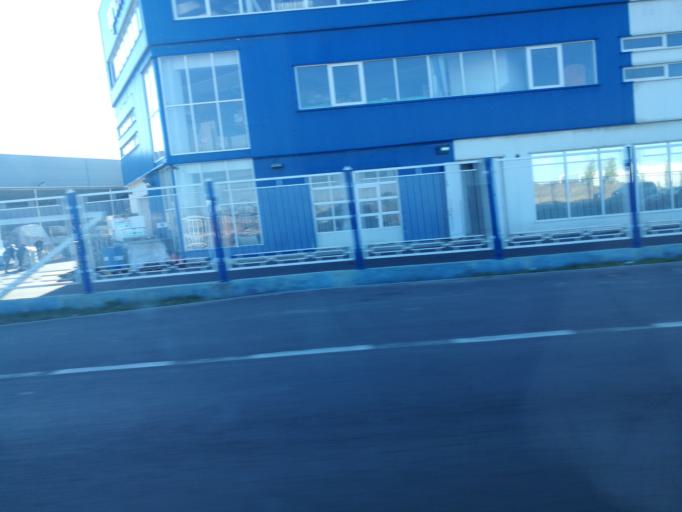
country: RO
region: Brasov
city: Brasov
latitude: 45.6803
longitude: 25.5859
